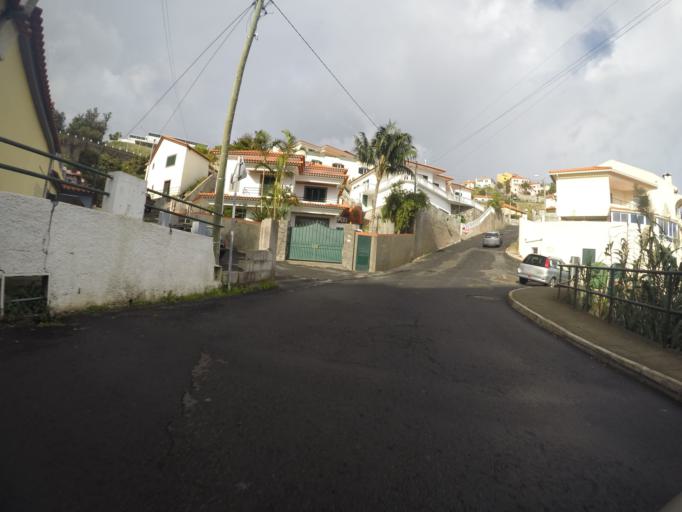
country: PT
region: Madeira
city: Canico
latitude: 32.6475
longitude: -16.8557
